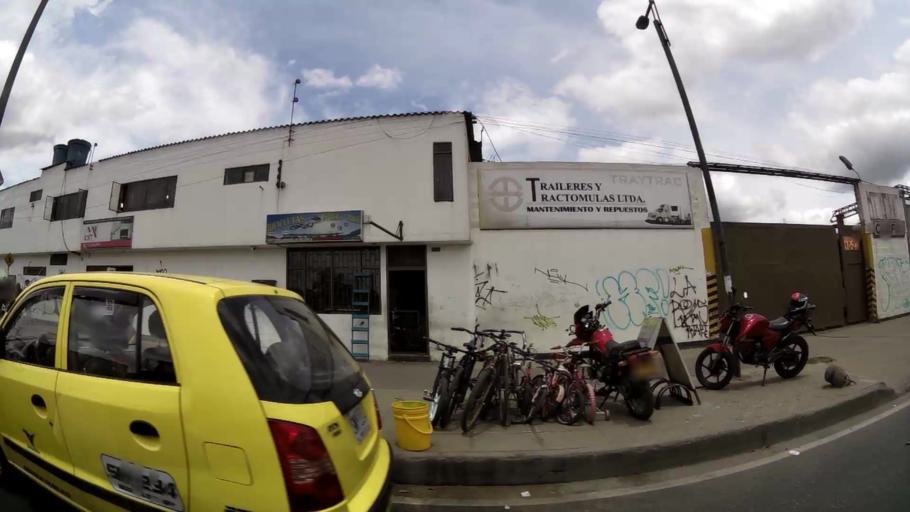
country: CO
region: Bogota D.C.
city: Bogota
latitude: 4.6496
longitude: -74.1468
